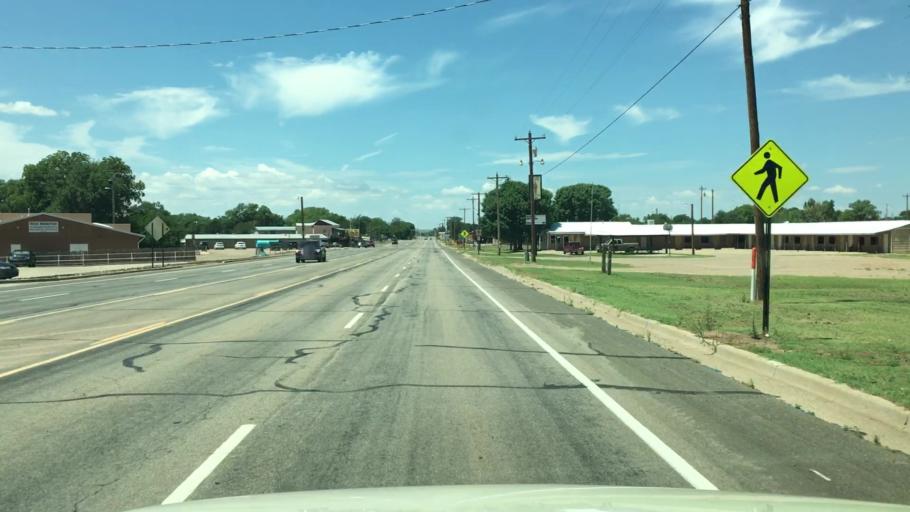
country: US
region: New Mexico
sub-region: De Baca County
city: Fort Sumner
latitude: 34.4659
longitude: -104.2270
